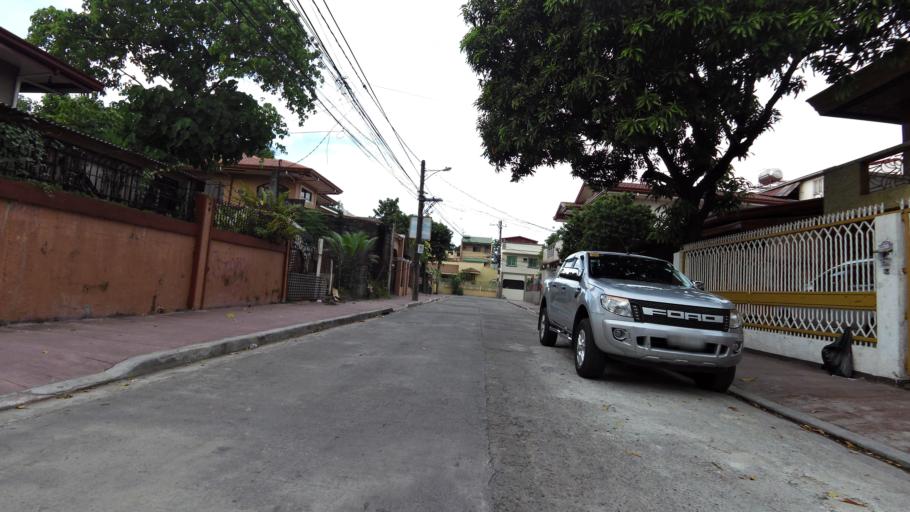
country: PH
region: Metro Manila
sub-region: Marikina
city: Calumpang
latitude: 14.6232
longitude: 121.1038
